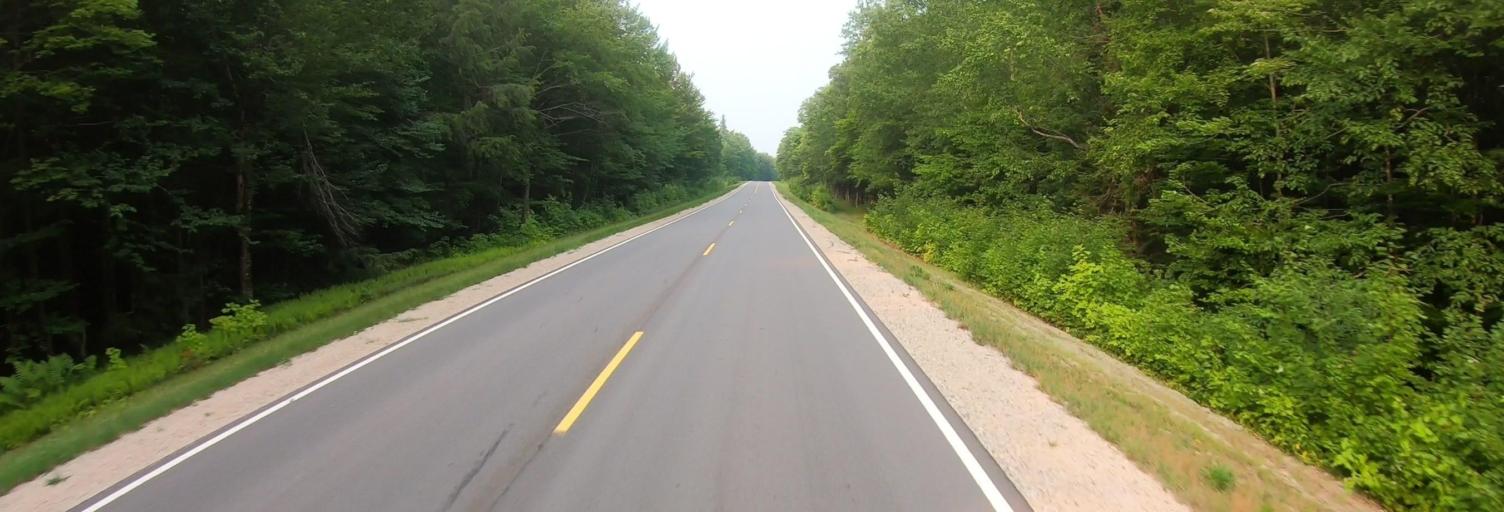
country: US
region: Michigan
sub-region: Luce County
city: Newberry
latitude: 46.4838
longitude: -85.0544
